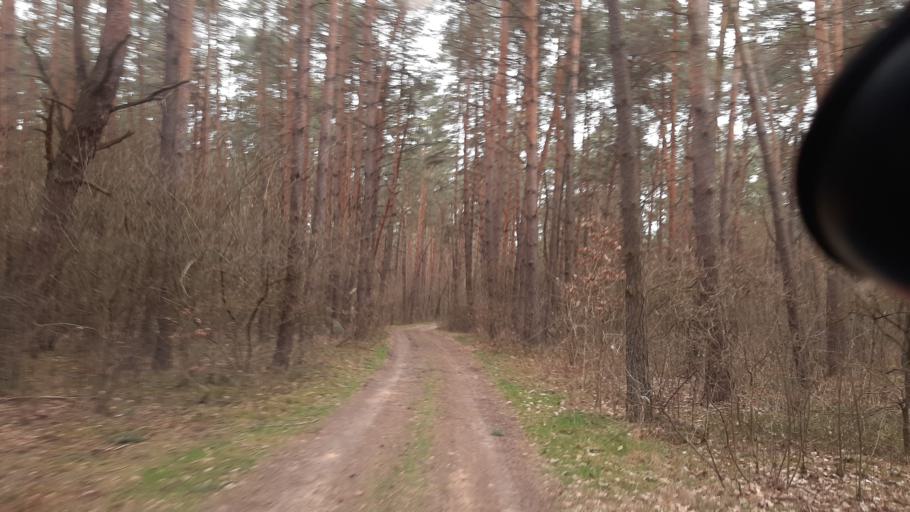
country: PL
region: Lublin Voivodeship
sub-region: Powiat lubartowski
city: Abramow
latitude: 51.4305
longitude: 22.3496
